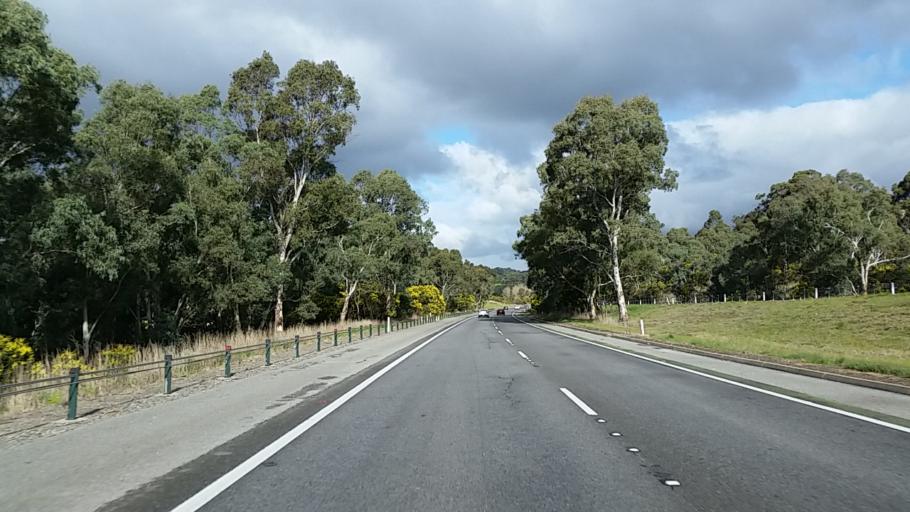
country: AU
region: South Australia
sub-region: Mount Barker
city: Hahndorf
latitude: -35.0343
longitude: 138.8100
